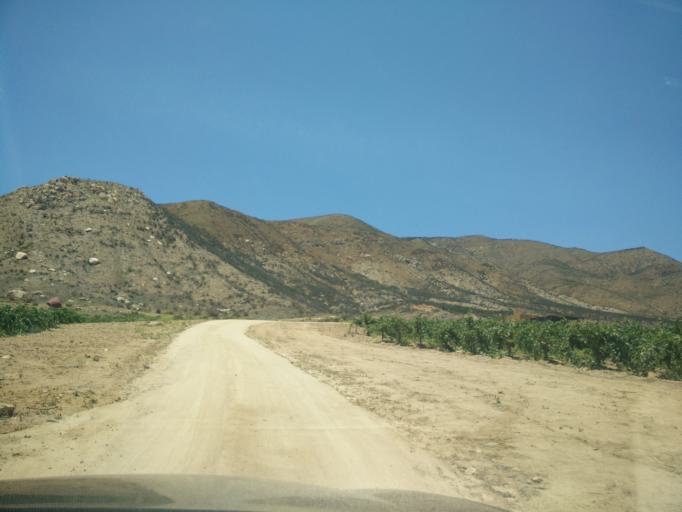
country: MX
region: Baja California
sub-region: Ensenada
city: Rancho Verde
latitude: 32.0521
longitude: -116.6659
